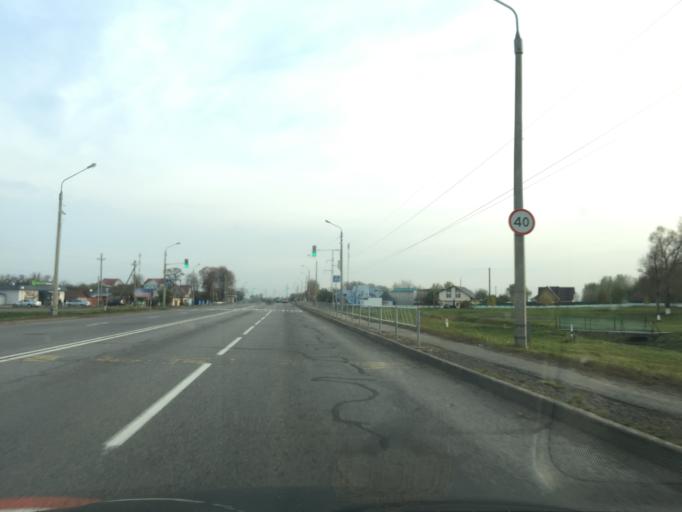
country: BY
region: Gomel
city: Kastsyukowka
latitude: 52.5092
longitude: 30.9438
